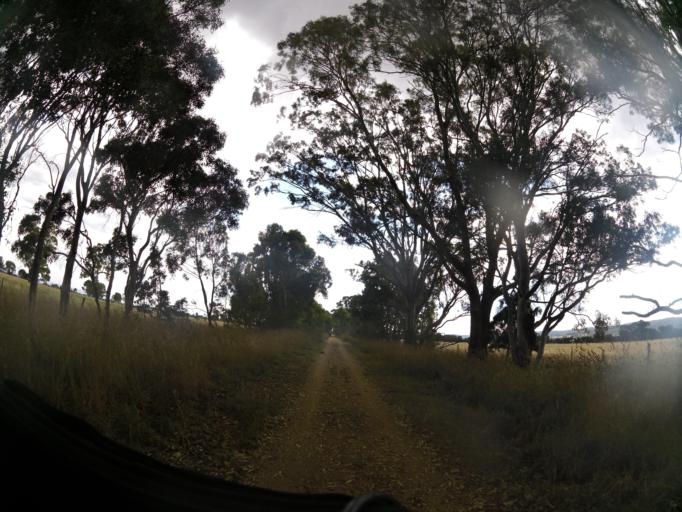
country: AU
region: Victoria
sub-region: Wellington
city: Heyfield
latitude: -38.0298
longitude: 146.6639
